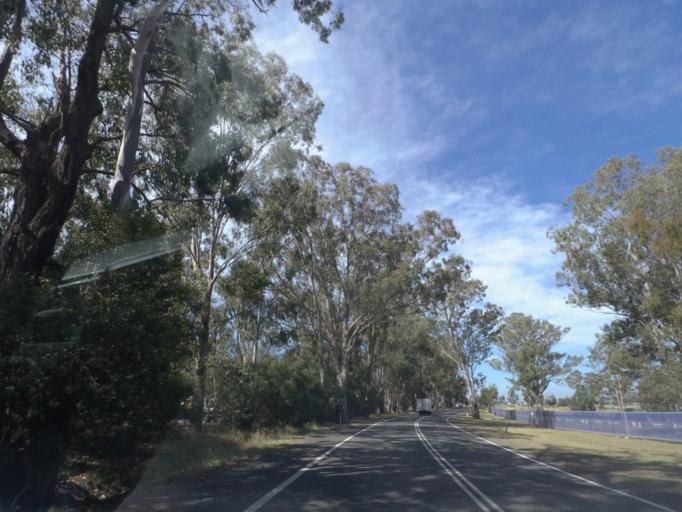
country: AU
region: New South Wales
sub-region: Campbelltown Municipality
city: Denham Court
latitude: -33.9767
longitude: 150.8511
